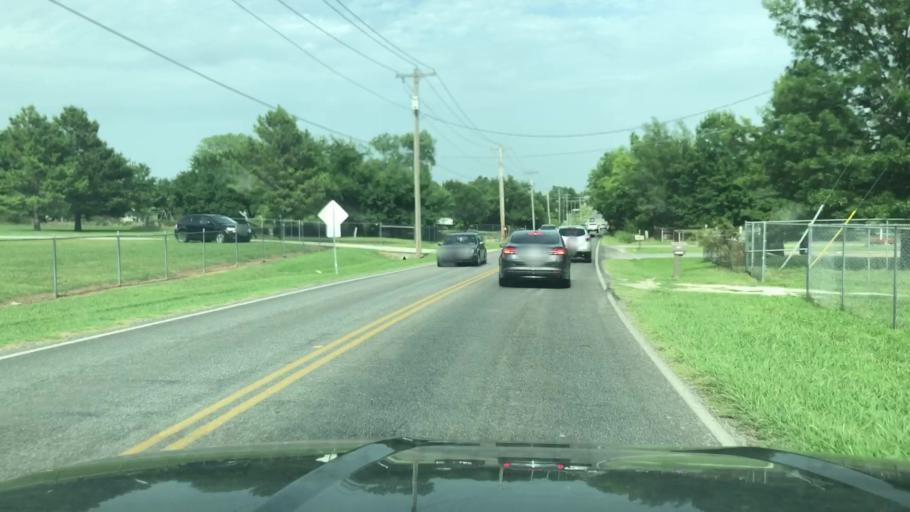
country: US
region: Oklahoma
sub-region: Tulsa County
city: Oakhurst
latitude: 36.0901
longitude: -96.0686
